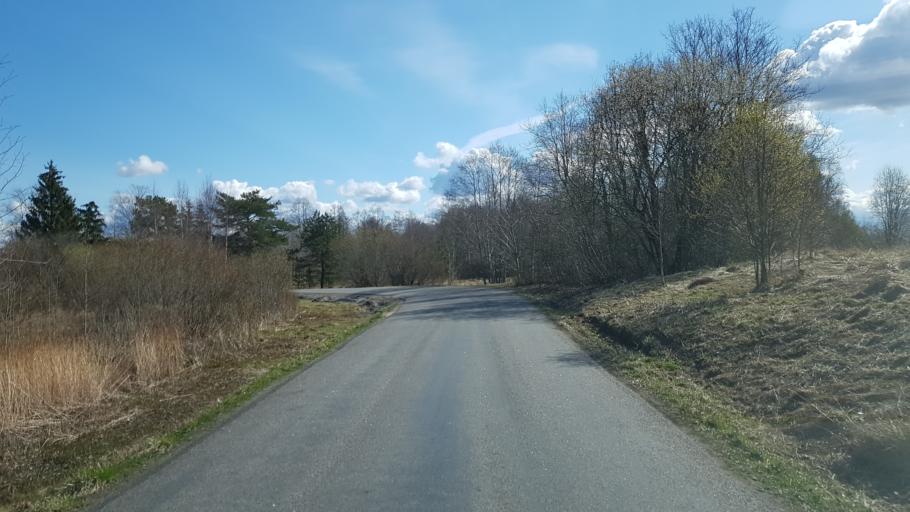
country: EE
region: Ida-Virumaa
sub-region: Narva-Joesuu linn
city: Narva-Joesuu
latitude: 59.4128
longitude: 28.0602
